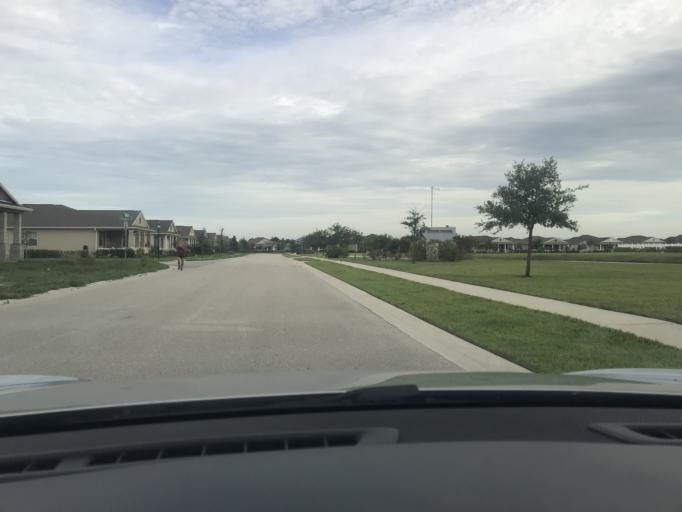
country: US
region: Florida
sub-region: Indian River County
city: West Vero Corridor
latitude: 27.6292
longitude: -80.4740
